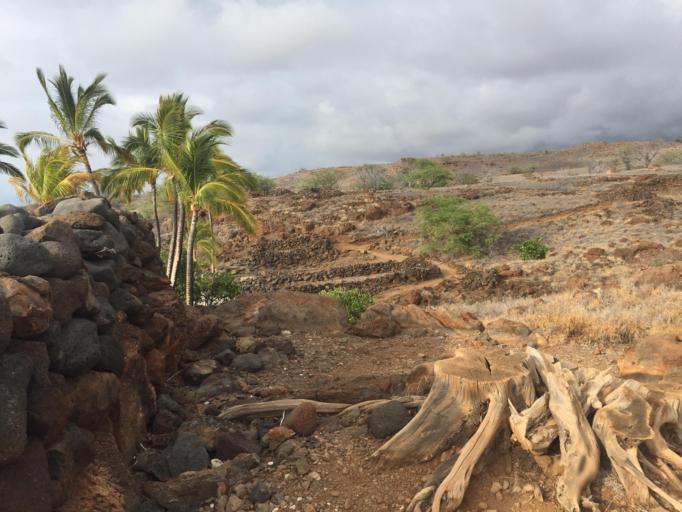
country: US
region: Hawaii
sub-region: Hawaii County
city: Hawi
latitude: 20.1759
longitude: -155.8999
